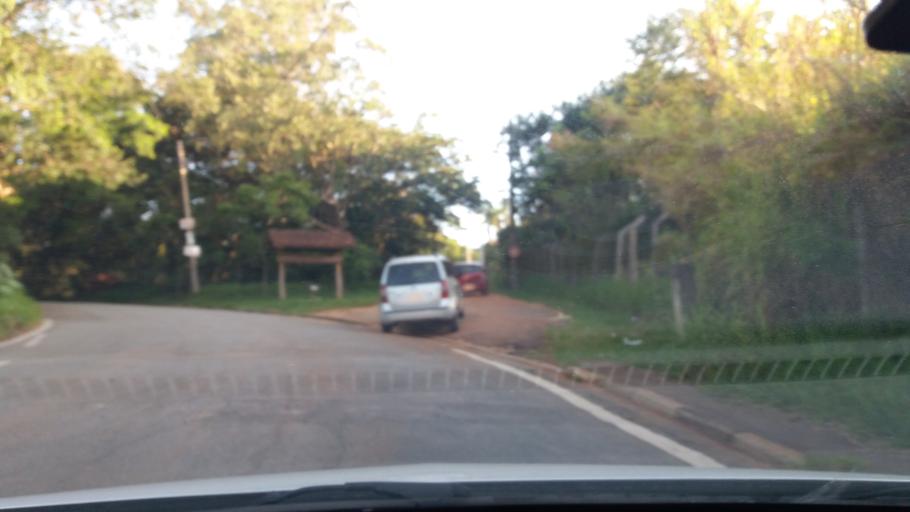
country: BR
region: Sao Paulo
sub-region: Franco Da Rocha
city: Franco da Rocha
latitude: -23.3324
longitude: -46.6865
